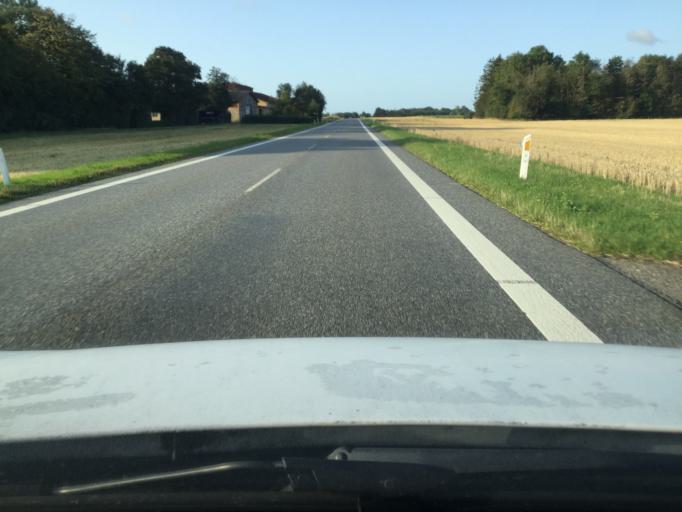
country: DK
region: Zealand
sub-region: Lolland Kommune
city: Rodby
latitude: 54.7316
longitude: 11.3887
